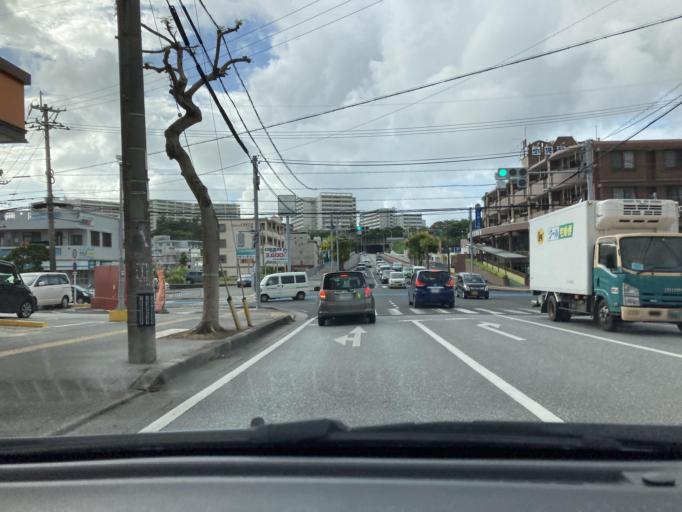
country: JP
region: Okinawa
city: Tomigusuku
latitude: 26.1837
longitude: 127.6765
